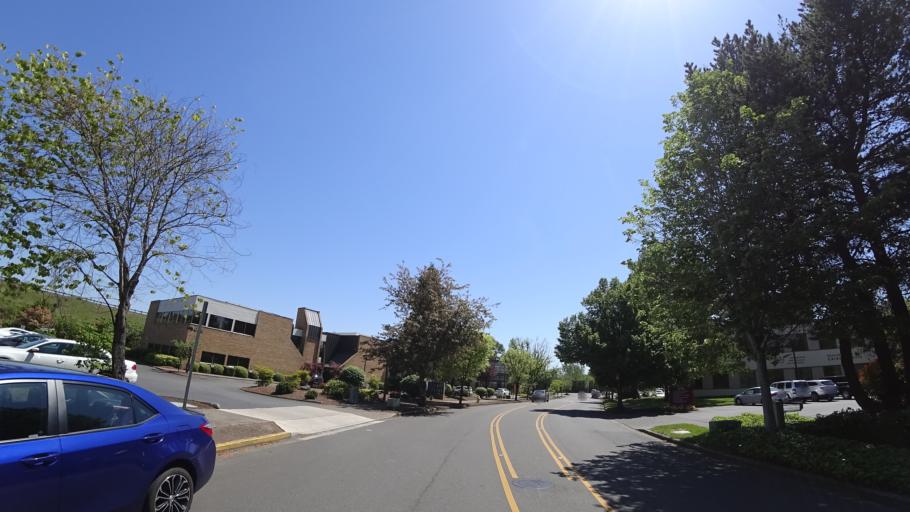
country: US
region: Oregon
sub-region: Washington County
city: Beaverton
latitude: 45.4834
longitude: -122.7947
